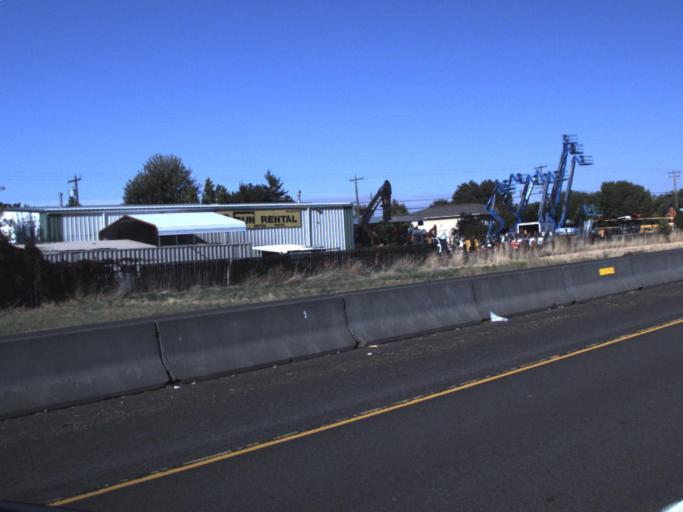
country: US
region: Washington
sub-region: Walla Walla County
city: Walla Walla
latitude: 46.0482
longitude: -118.3505
